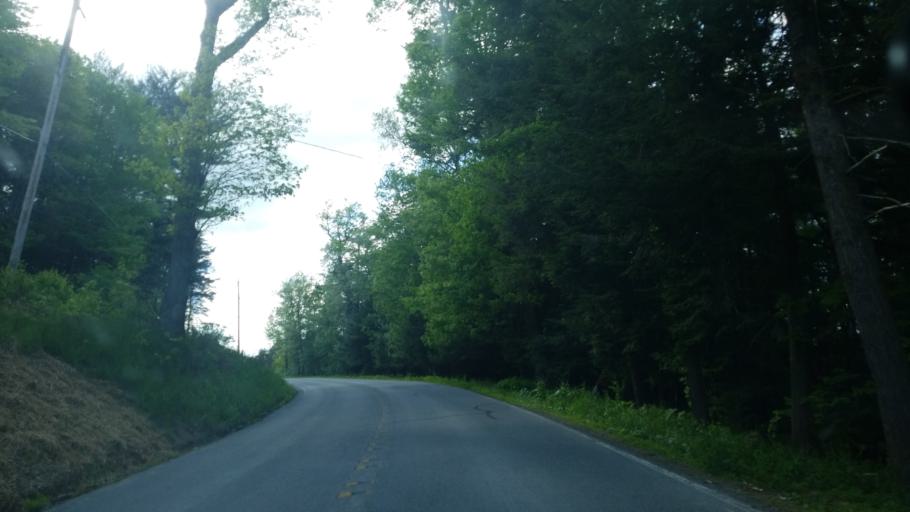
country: US
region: Pennsylvania
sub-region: Clearfield County
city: Hyde
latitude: 40.9738
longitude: -78.4426
